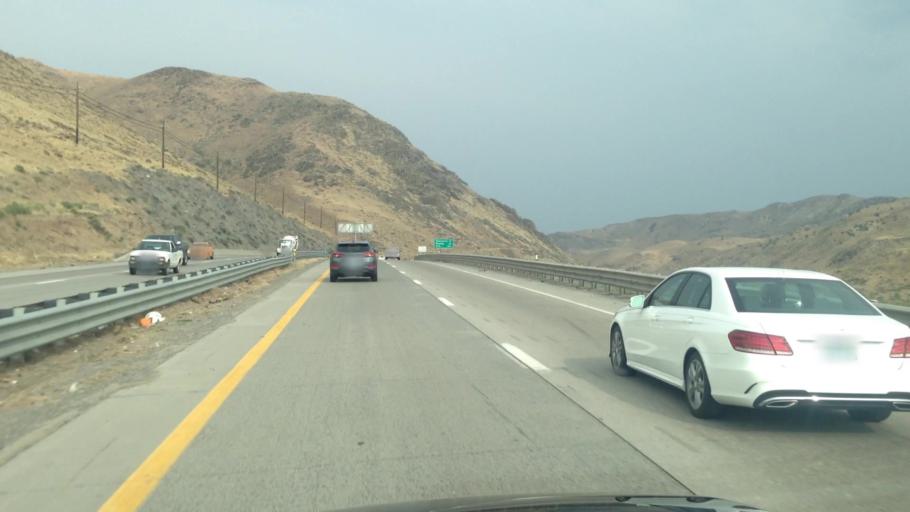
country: US
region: Nevada
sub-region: Washoe County
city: Sparks
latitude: 39.5238
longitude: -119.6929
